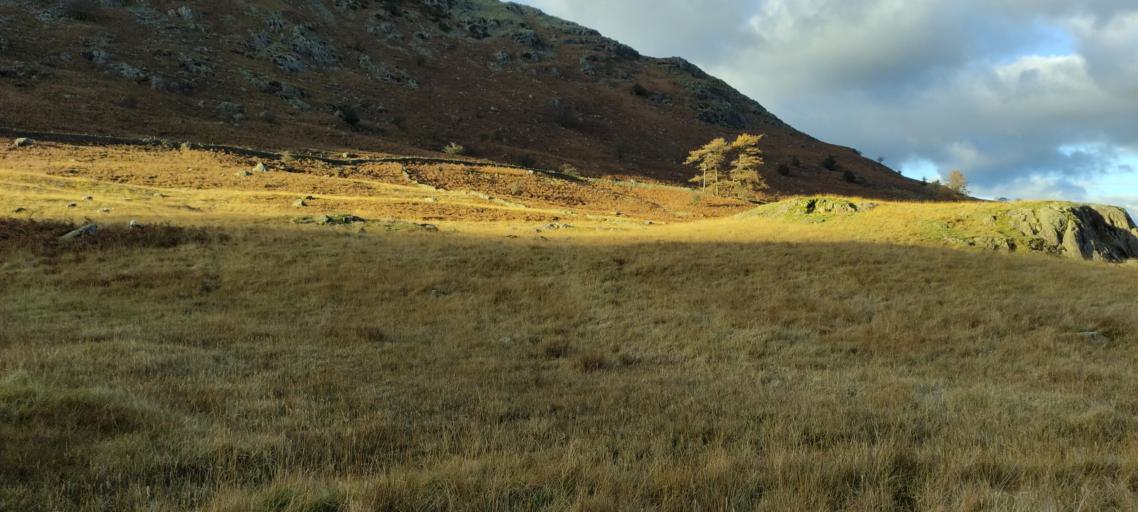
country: GB
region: England
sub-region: Cumbria
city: Ambleside
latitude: 54.5039
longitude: -3.0537
